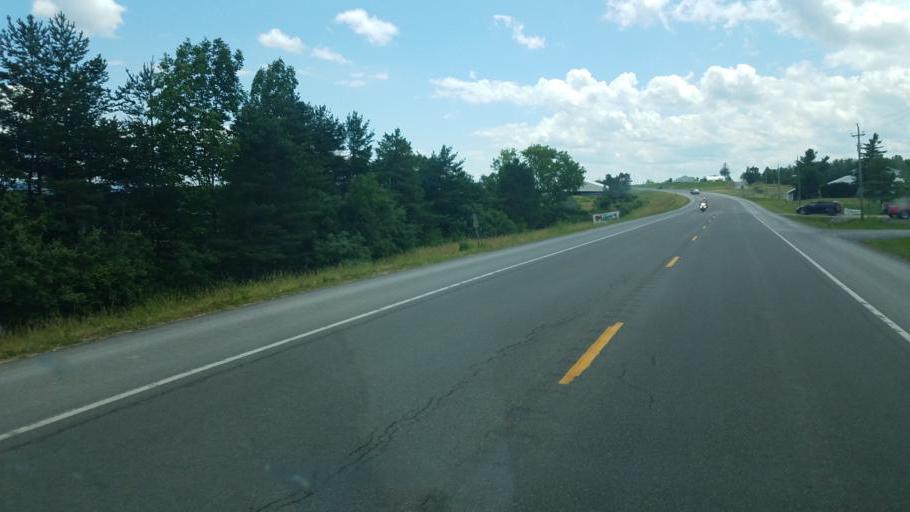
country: US
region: New York
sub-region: Yates County
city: Dundee
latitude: 42.5634
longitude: -77.0353
